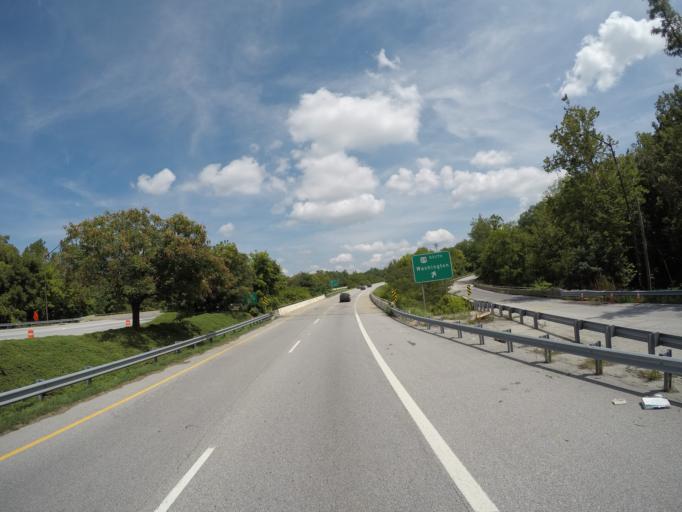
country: US
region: Maryland
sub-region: Howard County
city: Columbia
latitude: 39.2268
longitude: -76.8512
